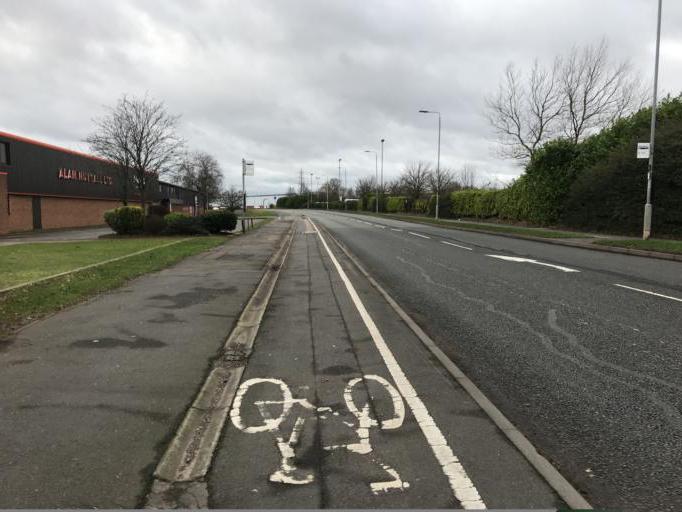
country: GB
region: England
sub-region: Leicestershire
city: Stoke Golding
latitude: 52.5405
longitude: -1.4077
